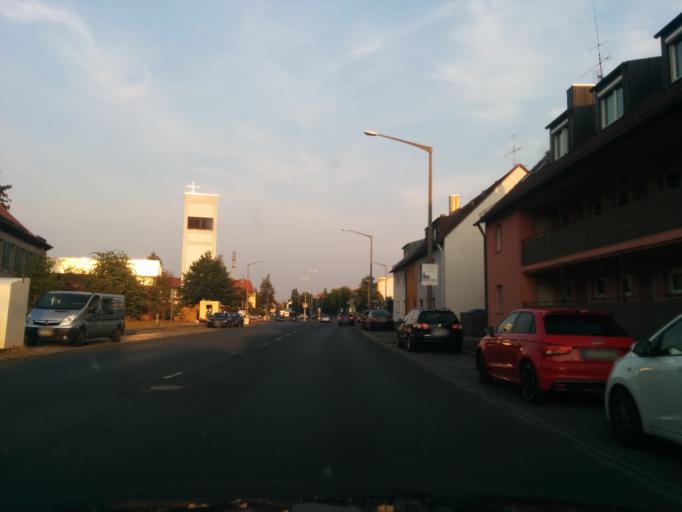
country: DE
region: Bavaria
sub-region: Regierungsbezirk Mittelfranken
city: Wetzendorf
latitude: 49.4700
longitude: 11.0268
